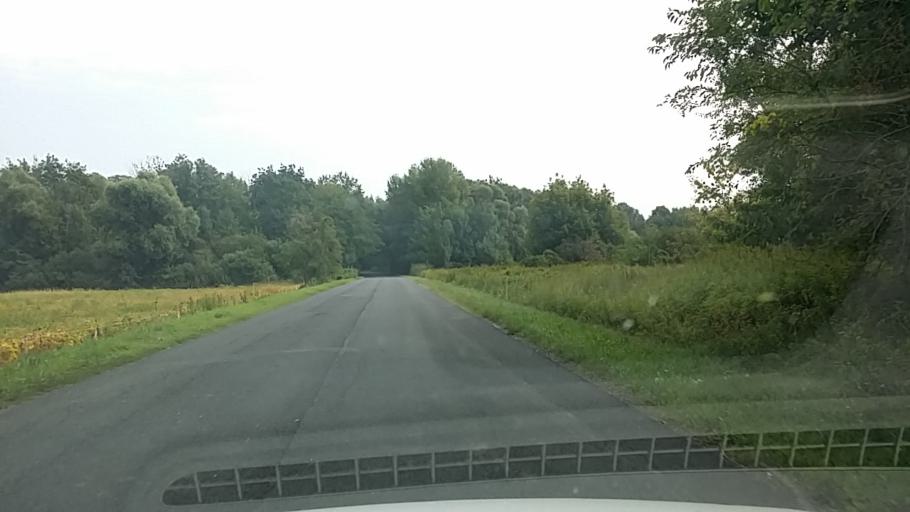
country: HU
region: Gyor-Moson-Sopron
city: Lebeny
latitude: 47.7272
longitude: 17.3206
